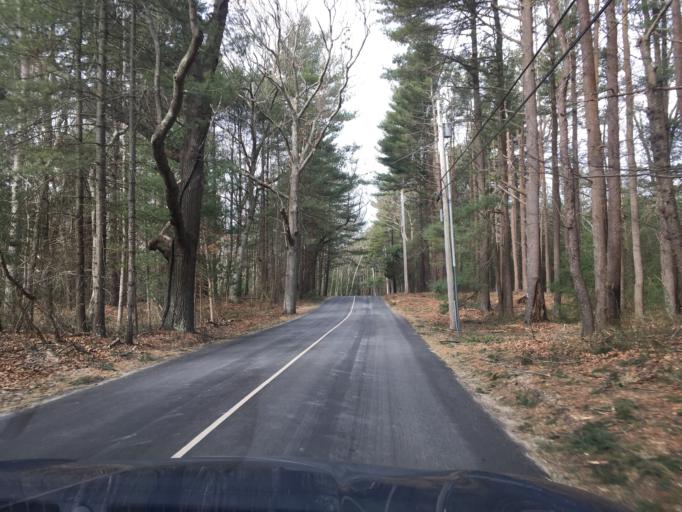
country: US
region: Rhode Island
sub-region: Kent County
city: East Greenwich
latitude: 41.6483
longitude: -71.4300
